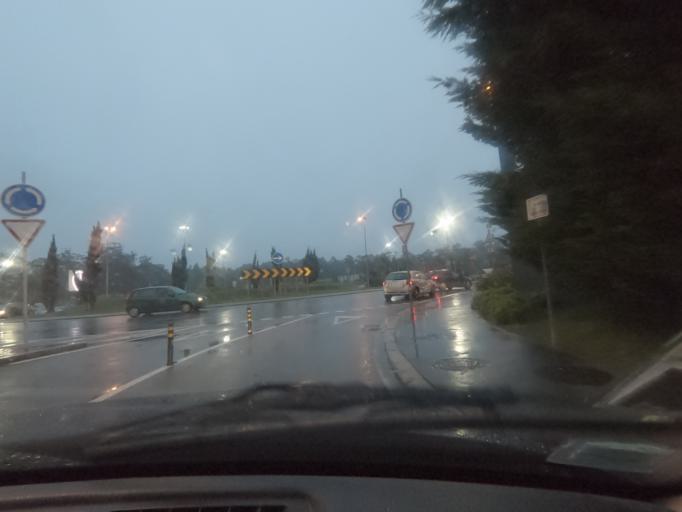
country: PT
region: Porto
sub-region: Vila do Conde
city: Arvore
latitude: 41.3012
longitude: -8.7081
